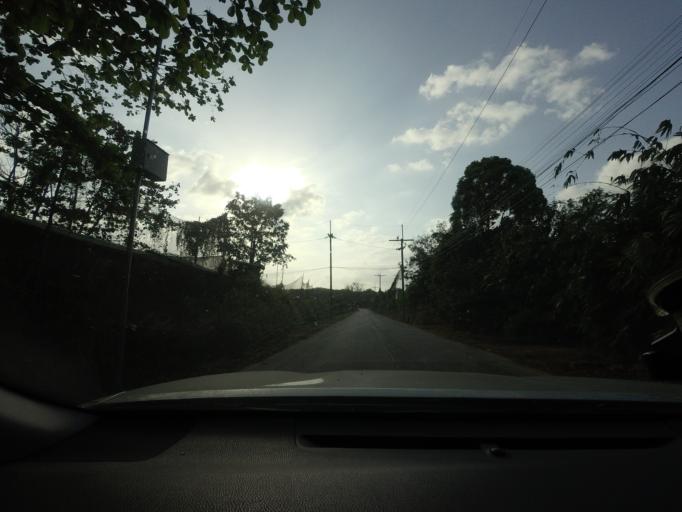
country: TH
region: Pattani
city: Mae Lan
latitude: 6.6158
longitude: 101.2397
